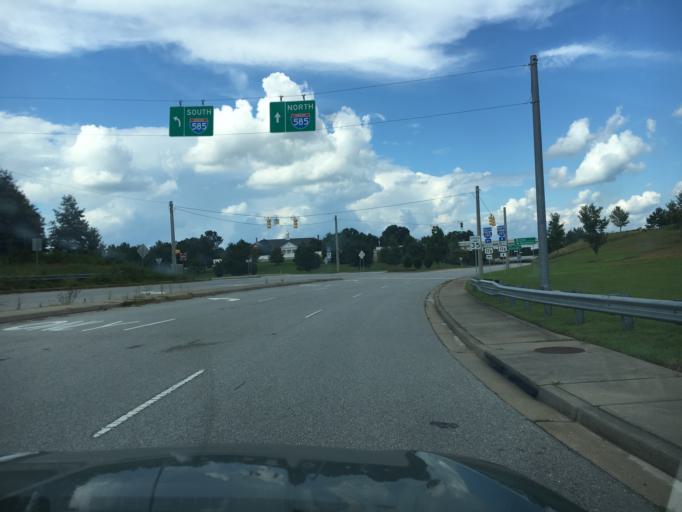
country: US
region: South Carolina
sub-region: Spartanburg County
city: Southern Shops
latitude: 34.9914
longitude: -81.9724
